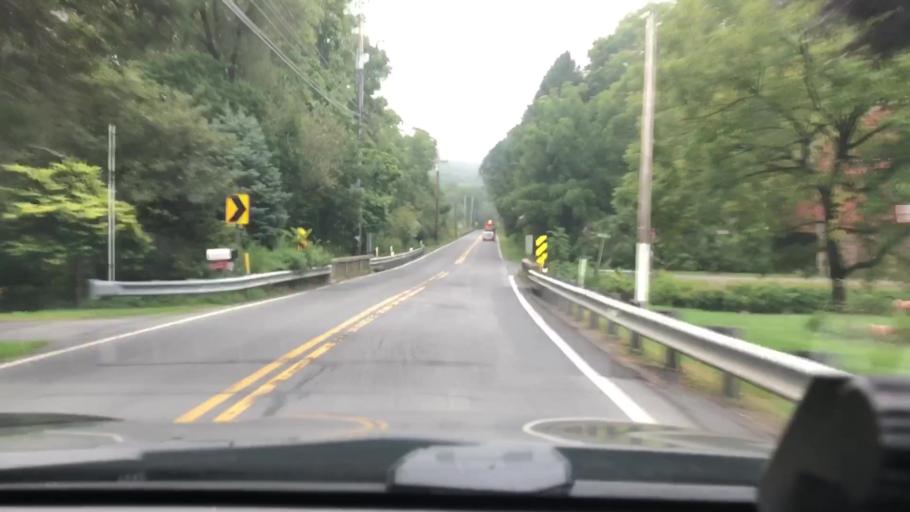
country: US
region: Pennsylvania
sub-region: Berks County
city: Kutztown
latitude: 40.5530
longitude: -75.8036
